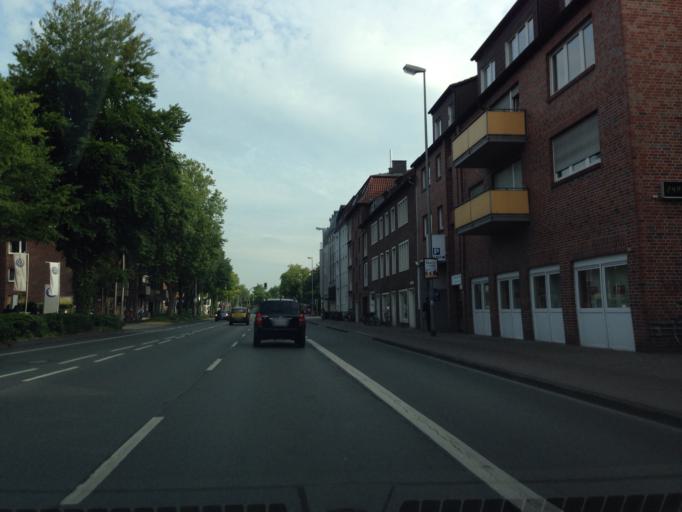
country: DE
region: North Rhine-Westphalia
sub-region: Regierungsbezirk Munster
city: Muenster
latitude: 51.9441
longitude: 7.6232
